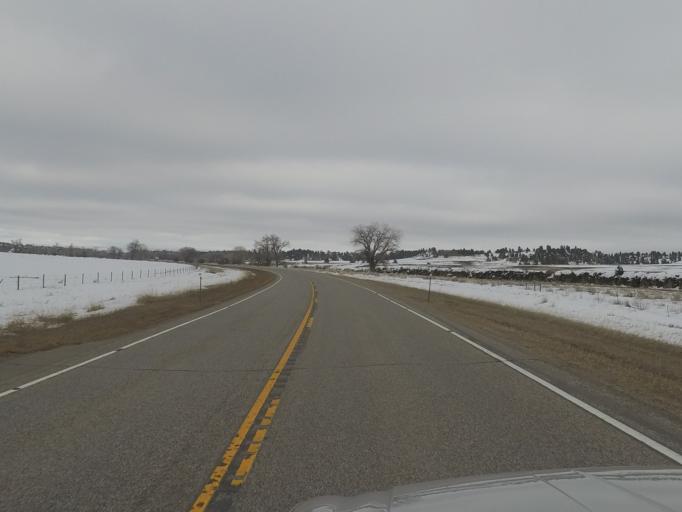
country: US
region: Montana
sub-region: Golden Valley County
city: Ryegate
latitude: 46.3014
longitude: -109.1103
